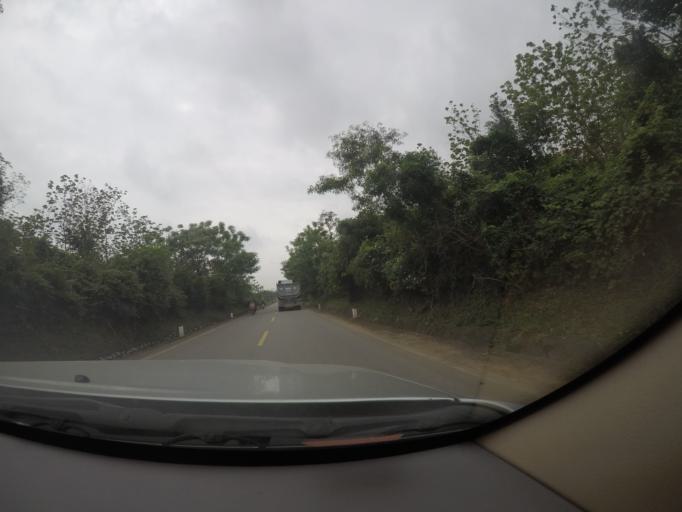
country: VN
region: Quang Binh
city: Hoan Lao
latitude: 17.5553
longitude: 106.4521
